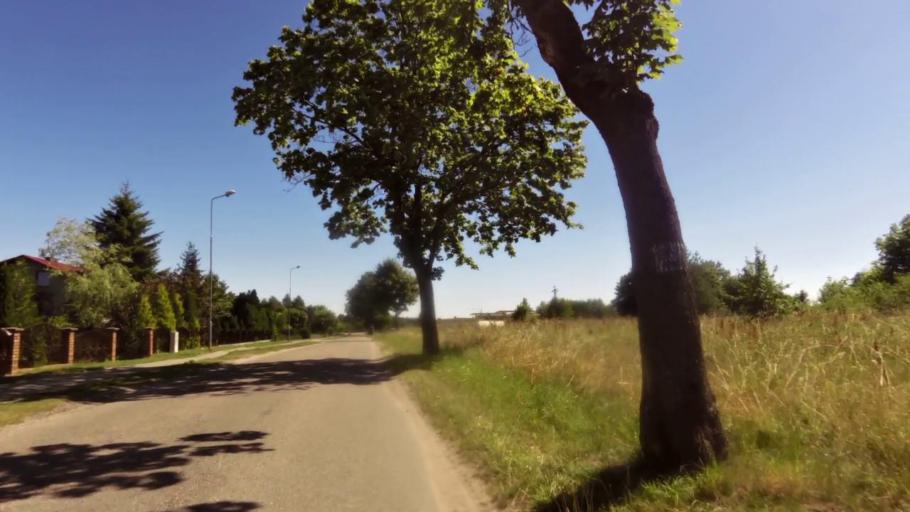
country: PL
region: West Pomeranian Voivodeship
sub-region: Powiat szczecinecki
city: Bialy Bor
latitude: 53.8949
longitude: 16.8469
